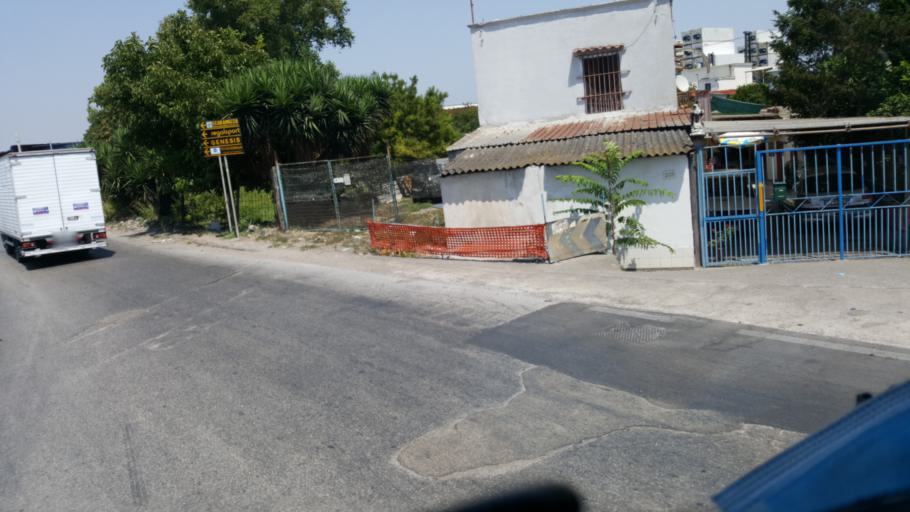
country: IT
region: Campania
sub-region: Provincia di Napoli
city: Arpino
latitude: 40.8511
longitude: 14.2996
